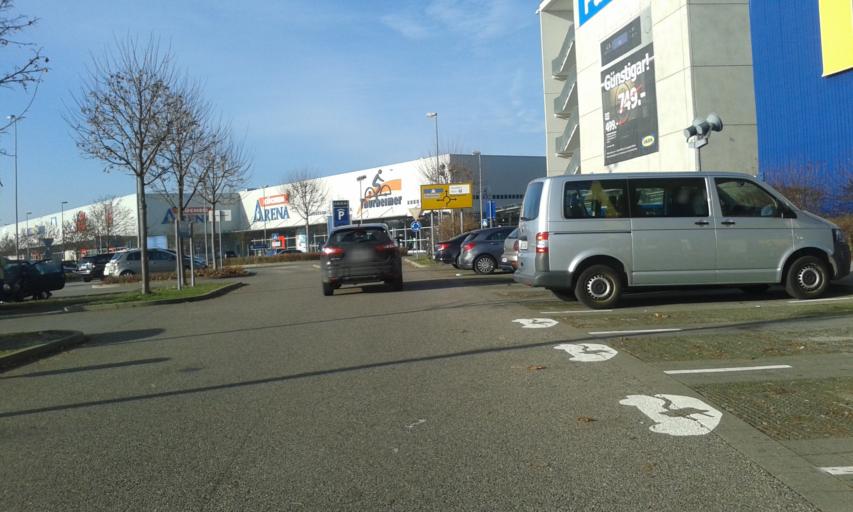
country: DE
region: Baden-Wuerttemberg
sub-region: Tuebingen Region
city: Ulm
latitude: 48.4035
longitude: 9.9762
